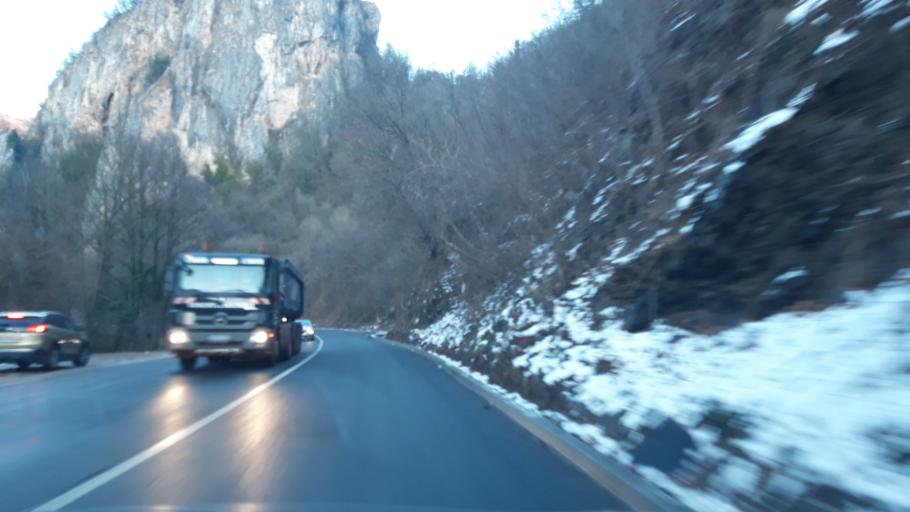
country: RS
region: Central Serbia
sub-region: Macvanski Okrug
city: Mali Zvornik
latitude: 44.2747
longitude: 19.1085
